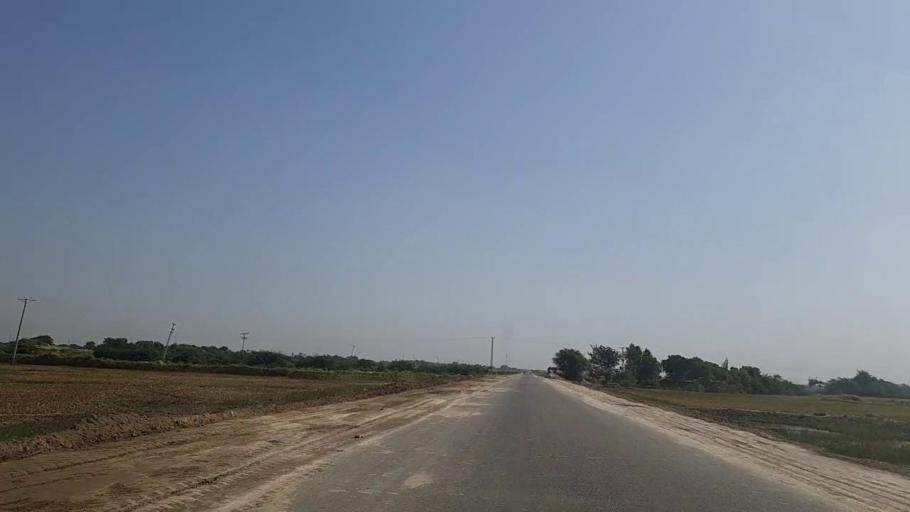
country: PK
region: Sindh
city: Mirpur Batoro
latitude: 24.7510
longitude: 68.2349
